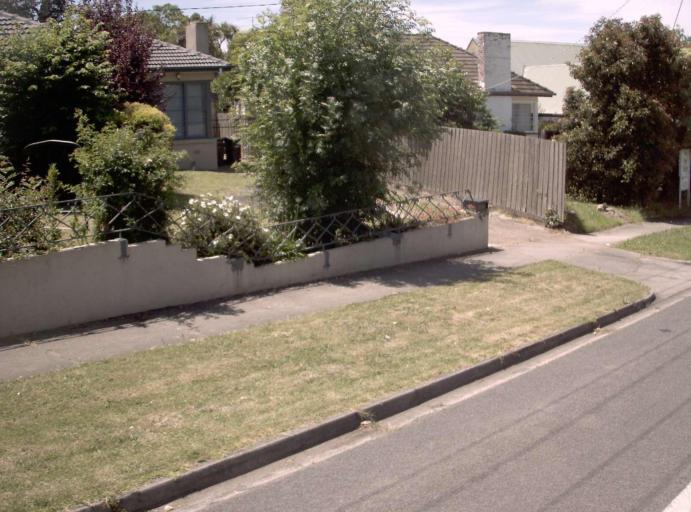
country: AU
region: Victoria
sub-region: Latrobe
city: Traralgon
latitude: -38.2014
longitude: 146.5257
